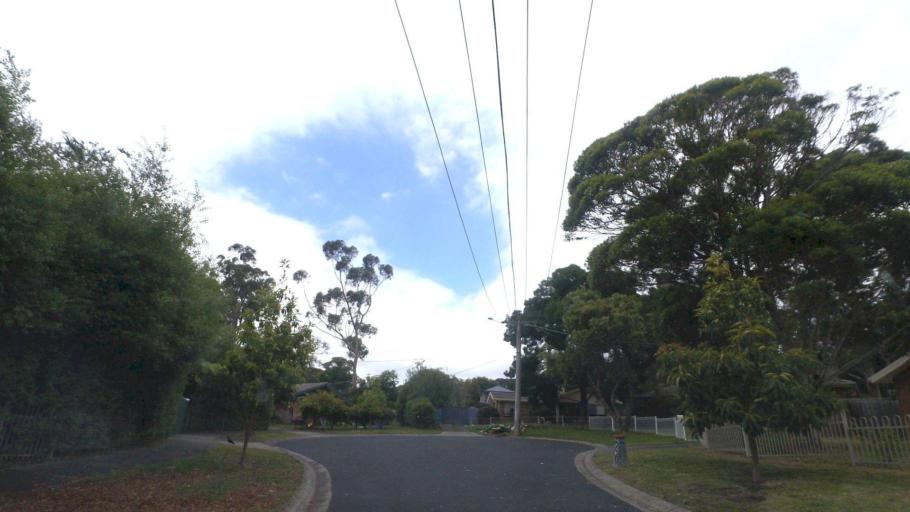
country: AU
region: Victoria
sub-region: Knox
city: The Basin
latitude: -37.8559
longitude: 145.3099
